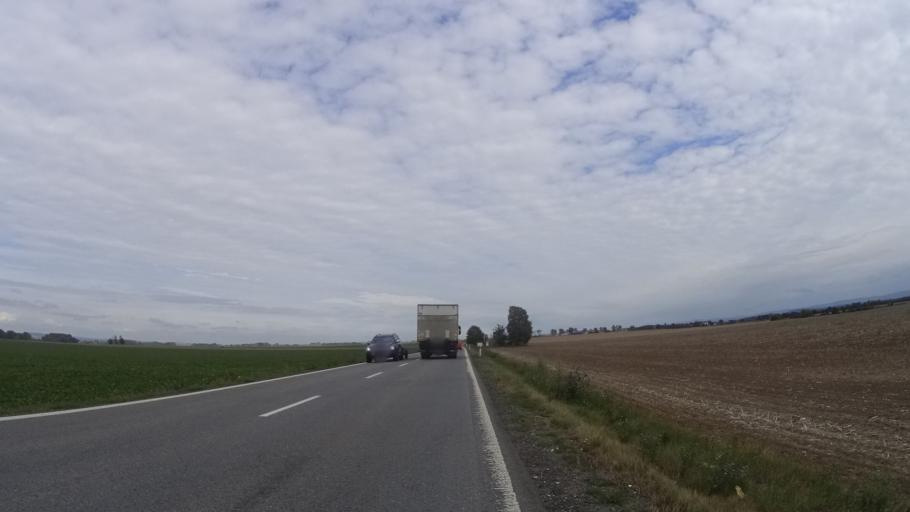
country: CZ
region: Olomoucky
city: Tovacov
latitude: 49.4442
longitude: 17.2801
